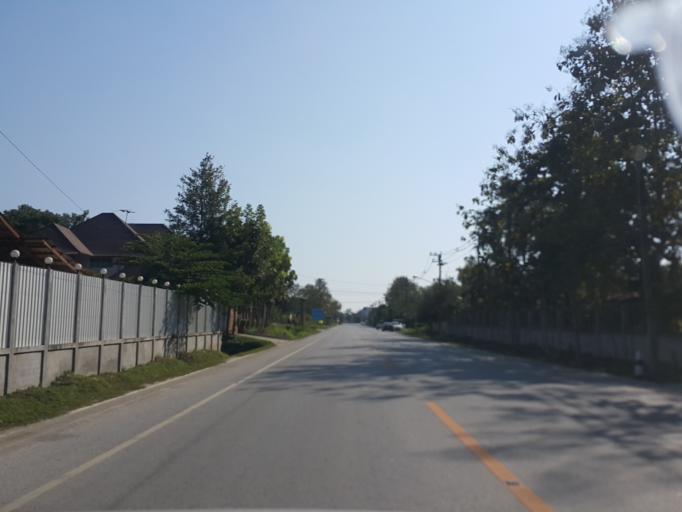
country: TH
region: Chiang Mai
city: San Sai
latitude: 18.8568
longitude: 99.1320
